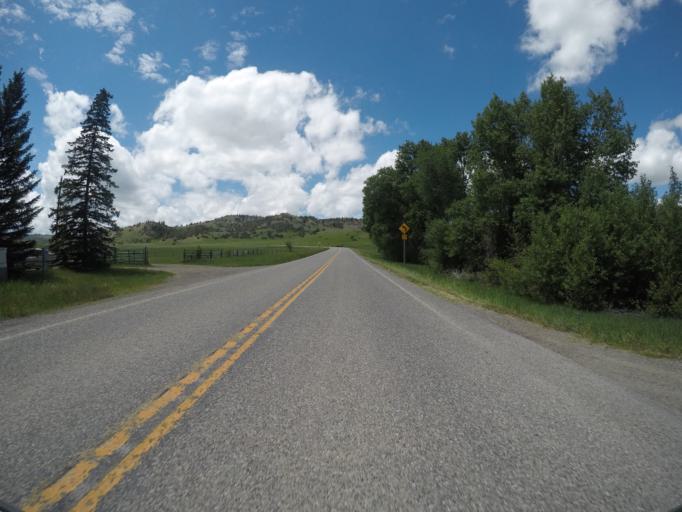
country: US
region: Montana
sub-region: Sweet Grass County
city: Big Timber
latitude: 45.6894
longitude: -110.0656
